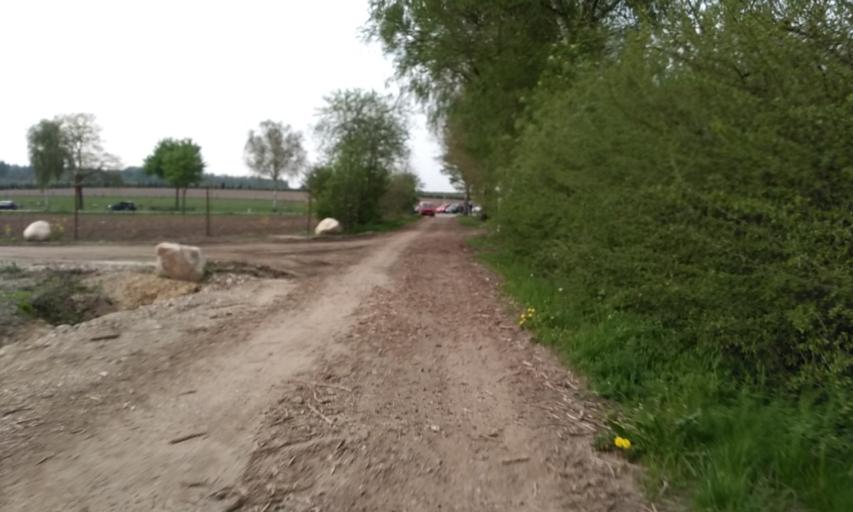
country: DE
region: Lower Saxony
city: Bliedersdorf
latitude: 53.4637
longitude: 9.5575
